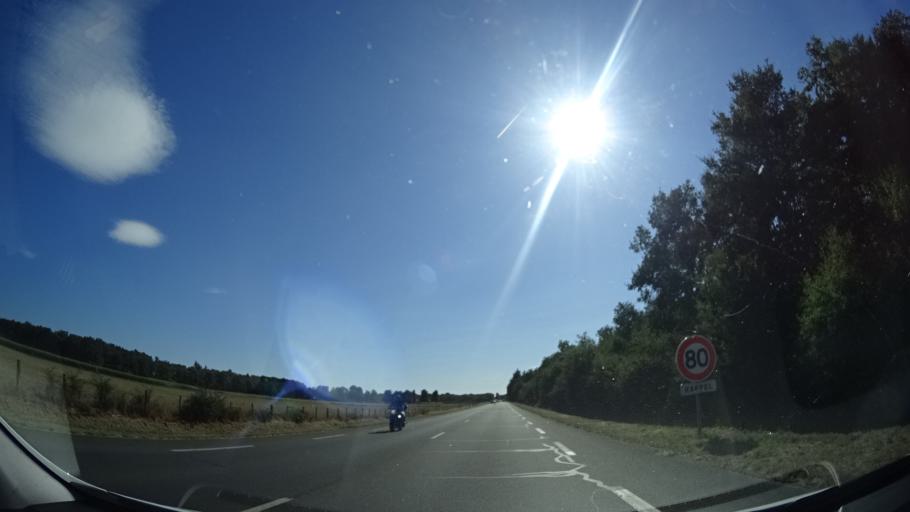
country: FR
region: Centre
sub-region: Departement du Loiret
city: Vitry-aux-Loges
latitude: 47.8988
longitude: 2.2817
